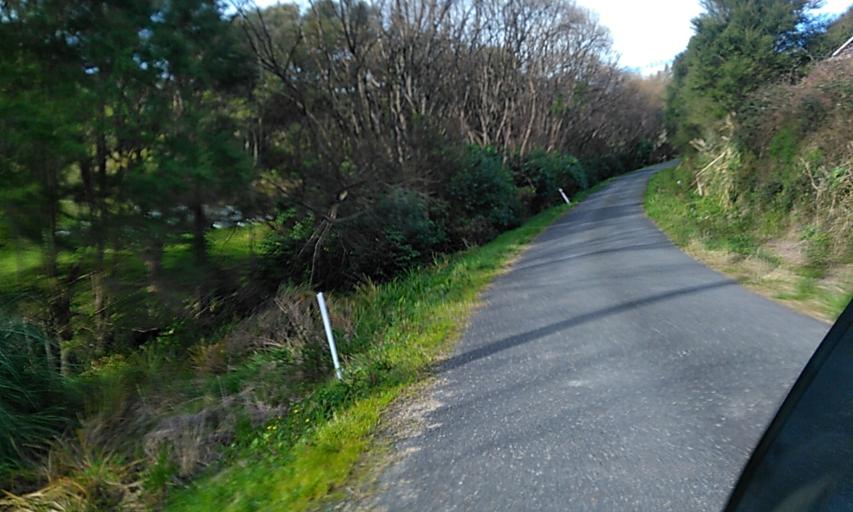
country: NZ
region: Gisborne
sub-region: Gisborne District
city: Gisborne
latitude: -38.6123
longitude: 178.0223
